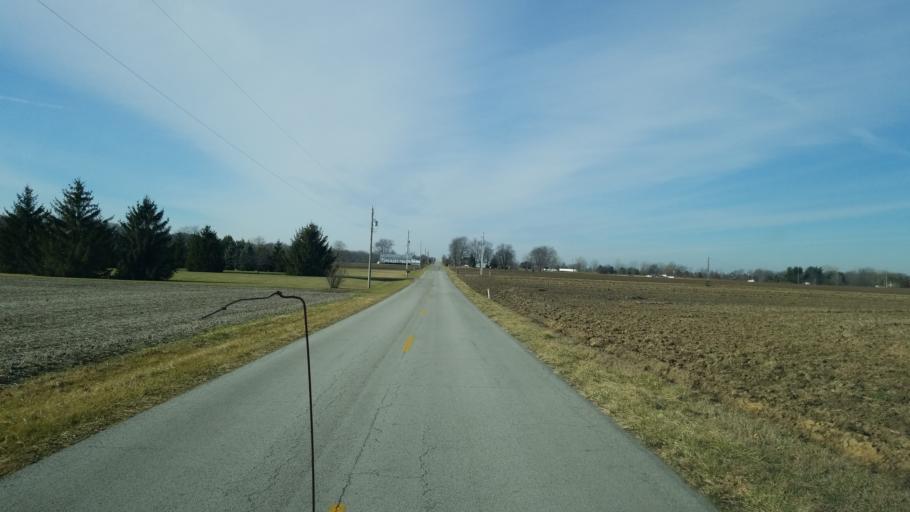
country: US
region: Ohio
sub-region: Allen County
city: Bluffton
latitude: 40.8629
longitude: -83.9199
